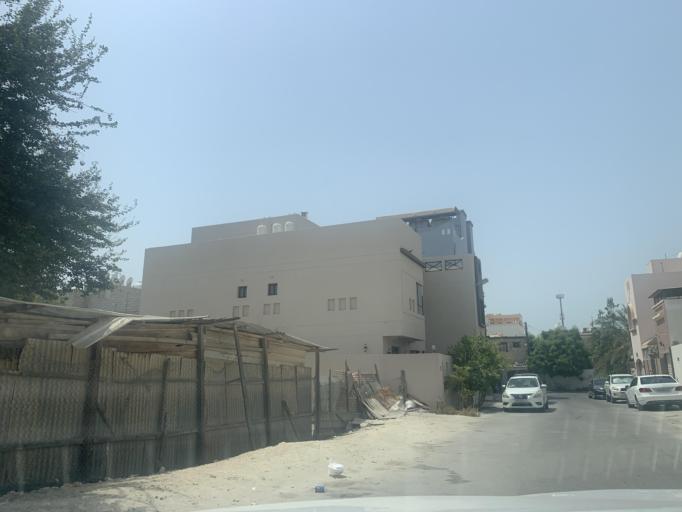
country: BH
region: Manama
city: Jidd Hafs
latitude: 26.2229
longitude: 50.4674
